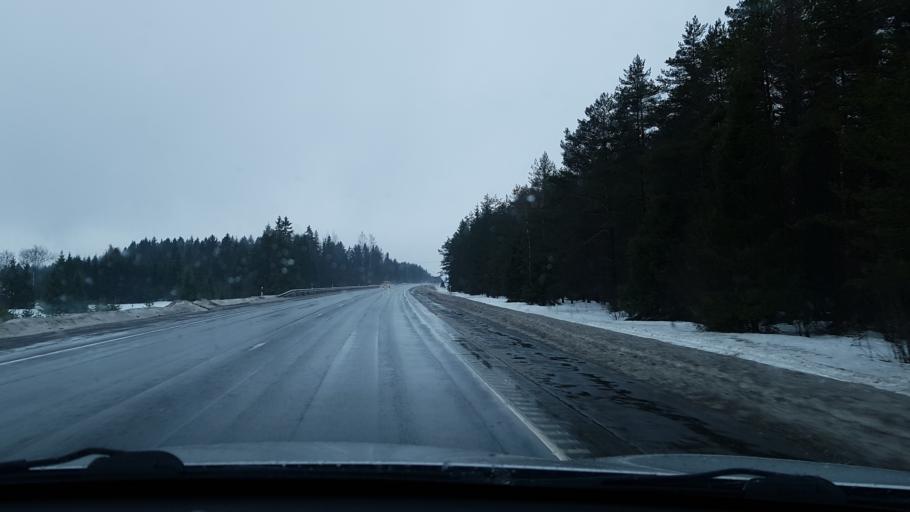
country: EE
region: Raplamaa
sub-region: Kohila vald
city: Kohila
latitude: 59.1886
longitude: 24.7872
